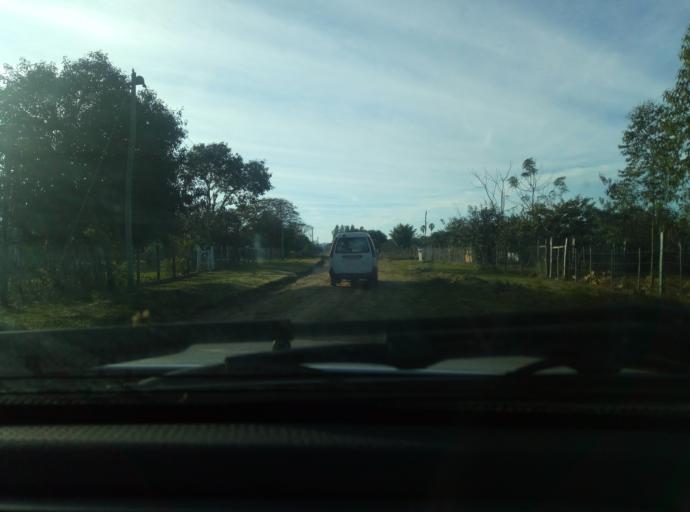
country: PY
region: Caaguazu
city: Carayao
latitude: -25.1922
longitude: -56.4086
